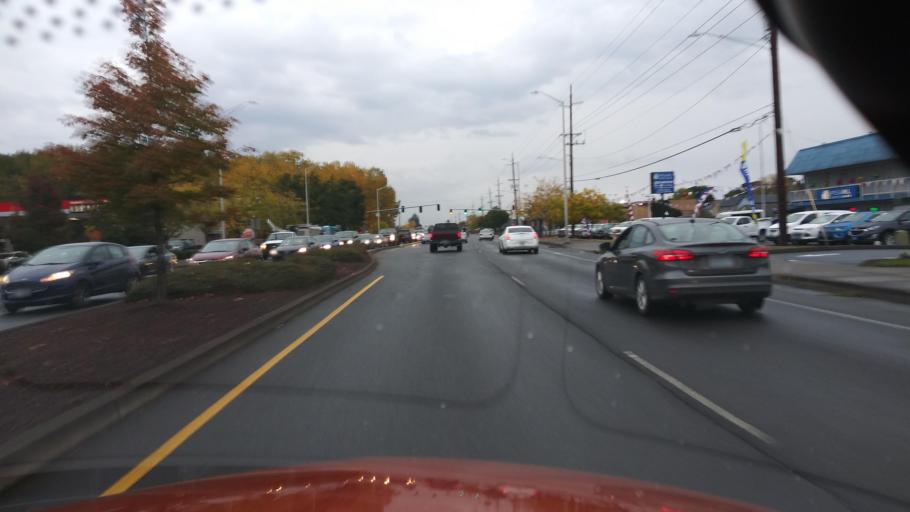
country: US
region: Oregon
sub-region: Washington County
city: Cornelius
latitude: 45.5202
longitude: -123.0457
